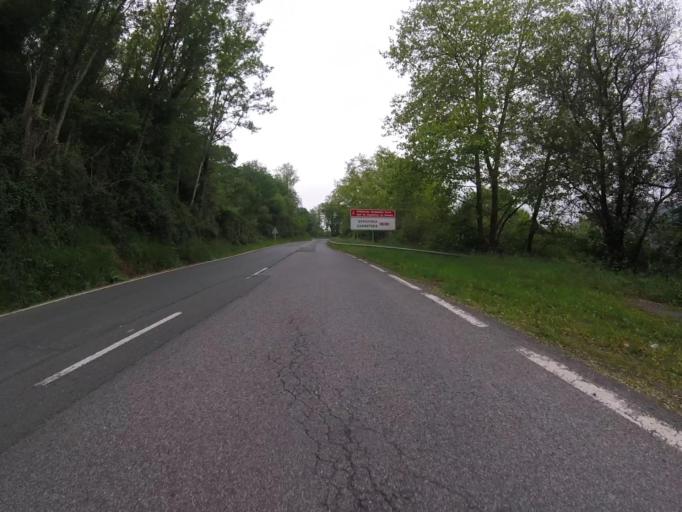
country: ES
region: Navarre
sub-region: Provincia de Navarra
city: Zugarramurdi
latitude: 43.2681
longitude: -1.4977
